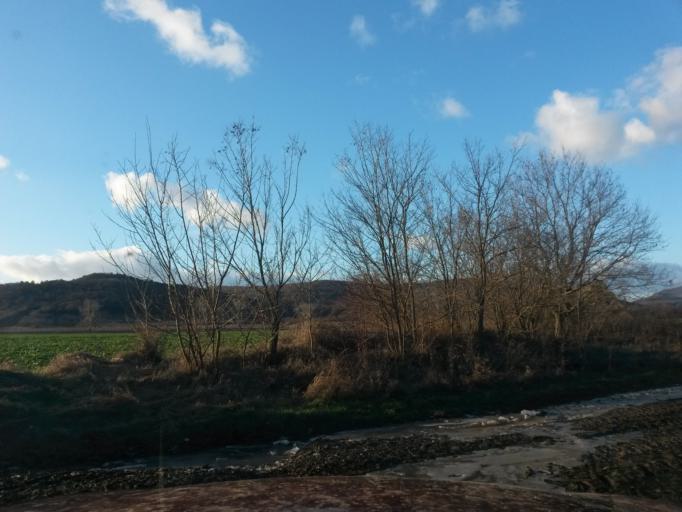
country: HU
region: Borsod-Abauj-Zemplen
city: Tolcsva
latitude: 48.2902
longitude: 21.5145
